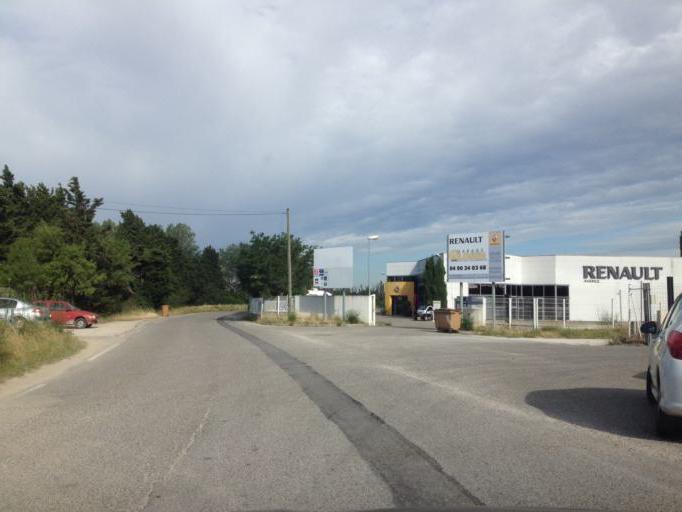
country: FR
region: Provence-Alpes-Cote d'Azur
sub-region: Departement du Vaucluse
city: Orange
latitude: 44.1216
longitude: 4.7981
